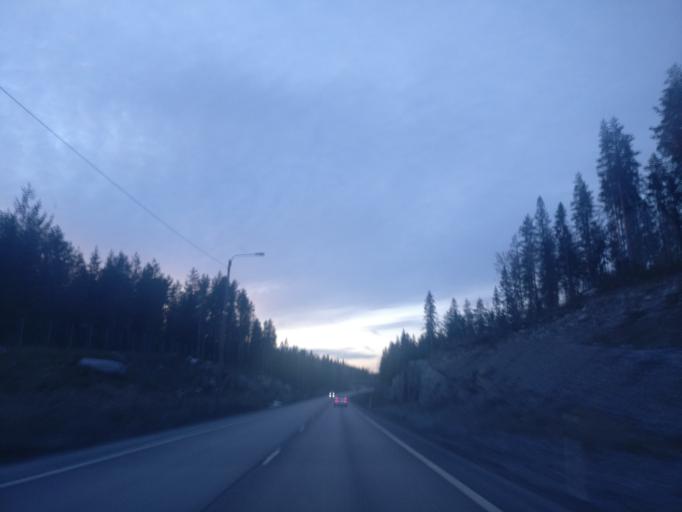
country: FI
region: Central Finland
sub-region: Jyvaeskylae
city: Saeynaetsalo
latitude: 62.1941
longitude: 25.8978
